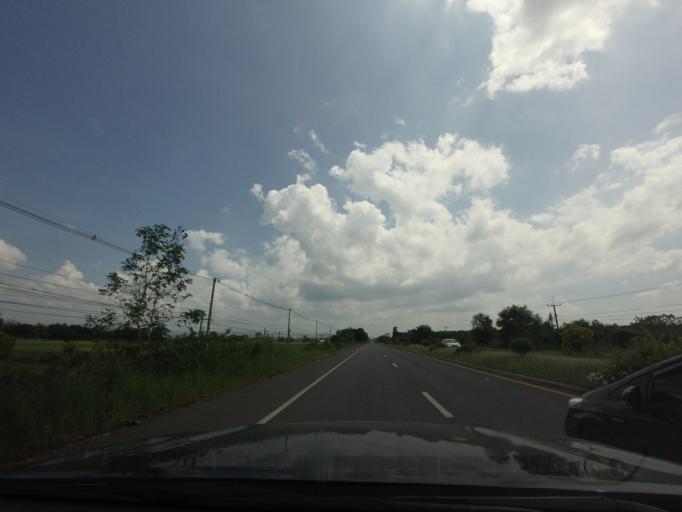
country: TH
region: Phetchabun
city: Phetchabun
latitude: 16.2412
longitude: 101.0765
